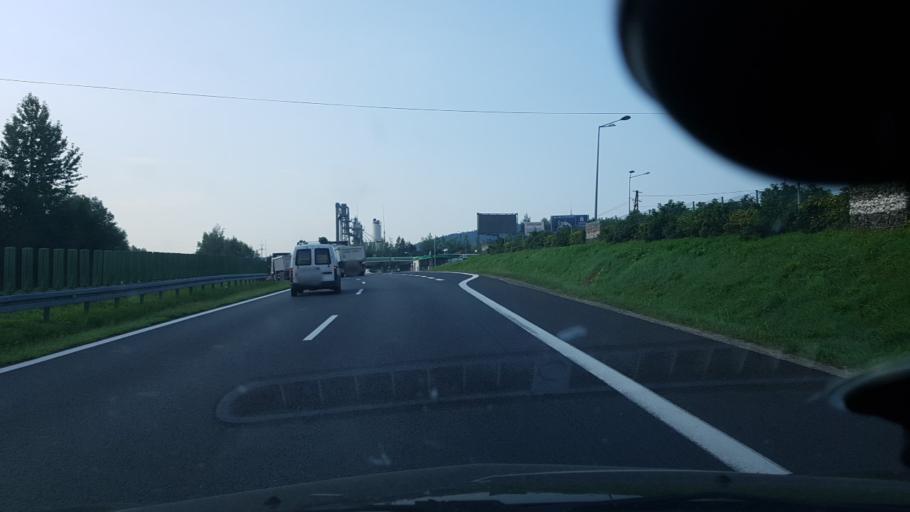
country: PL
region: Lesser Poland Voivodeship
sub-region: Powiat myslenicki
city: Jawornik
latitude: 49.8674
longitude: 19.9089
